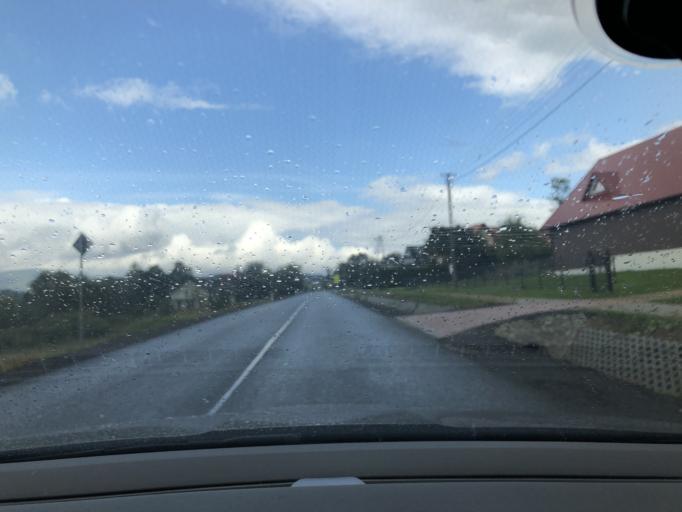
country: PL
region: Lesser Poland Voivodeship
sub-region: Powiat nowotarski
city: Zubrzyca Dolna
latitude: 49.5201
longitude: 19.6739
